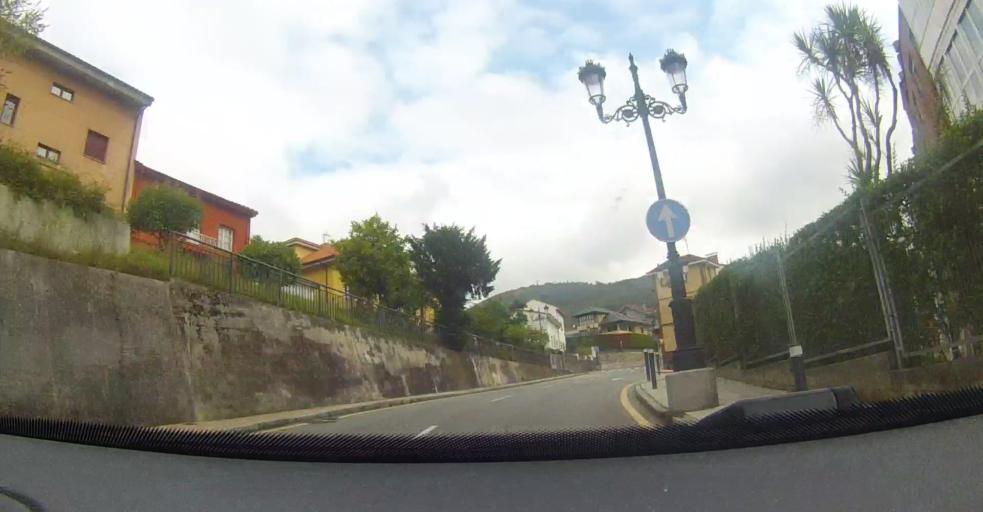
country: ES
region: Asturias
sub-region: Province of Asturias
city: Oviedo
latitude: 43.3706
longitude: -5.8577
